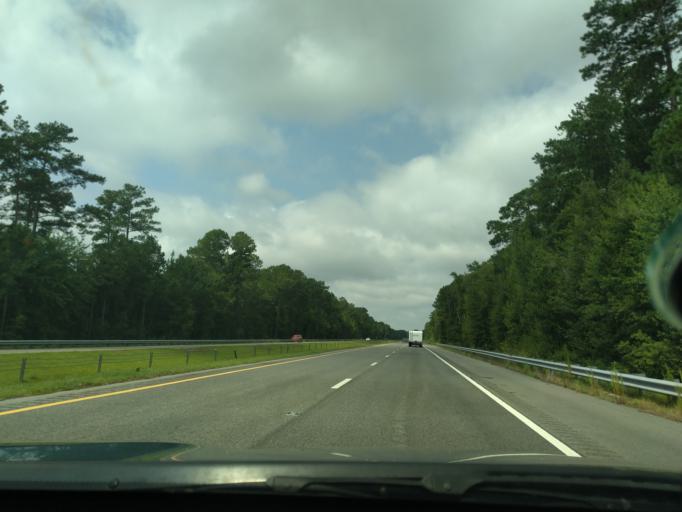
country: US
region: North Carolina
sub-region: Pitt County
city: Bethel
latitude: 35.8329
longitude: -77.3215
